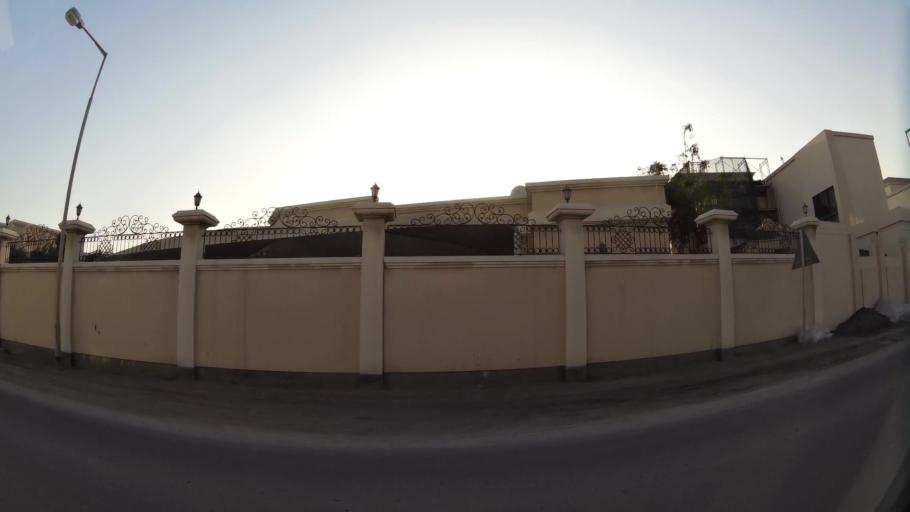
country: BH
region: Manama
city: Jidd Hafs
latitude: 26.2027
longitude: 50.4969
